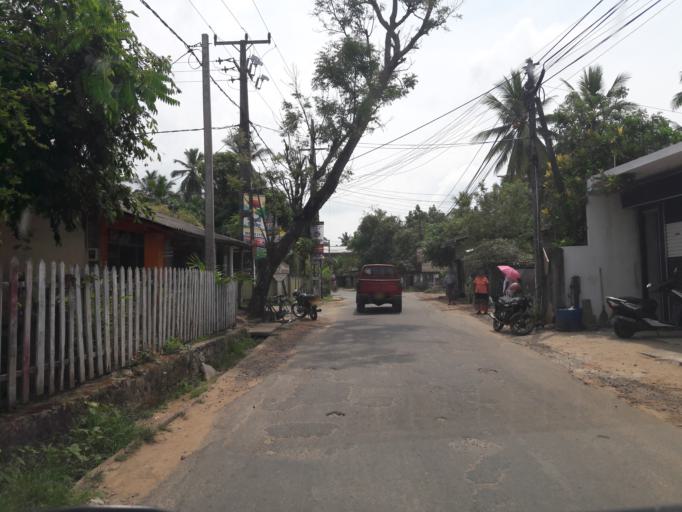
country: LK
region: Southern
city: Hikkaduwa
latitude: 6.0953
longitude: 80.1489
